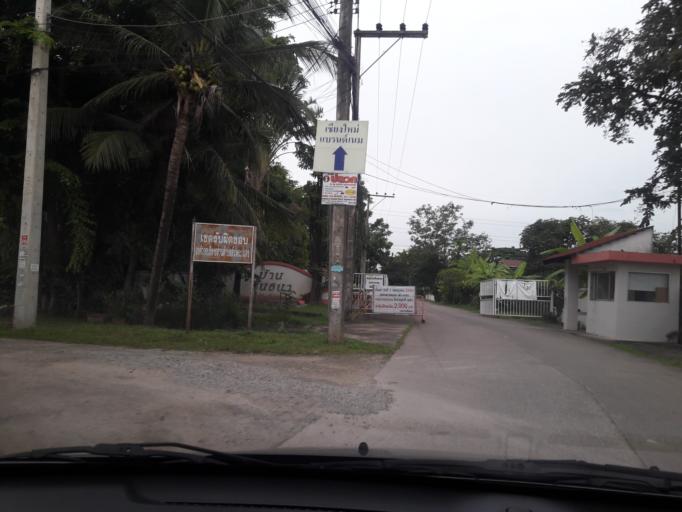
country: TH
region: Chiang Mai
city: San Sai
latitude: 18.8069
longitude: 99.0303
